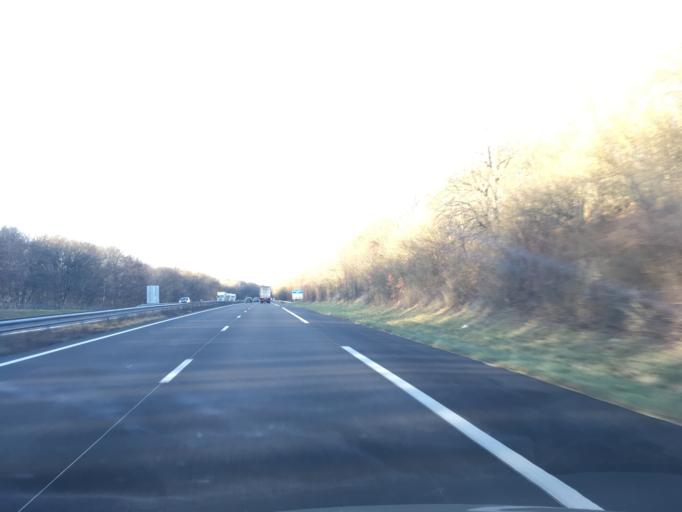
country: FR
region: Bourgogne
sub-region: Departement de l'Yonne
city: Joux-la-Ville
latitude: 47.5838
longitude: 3.9254
